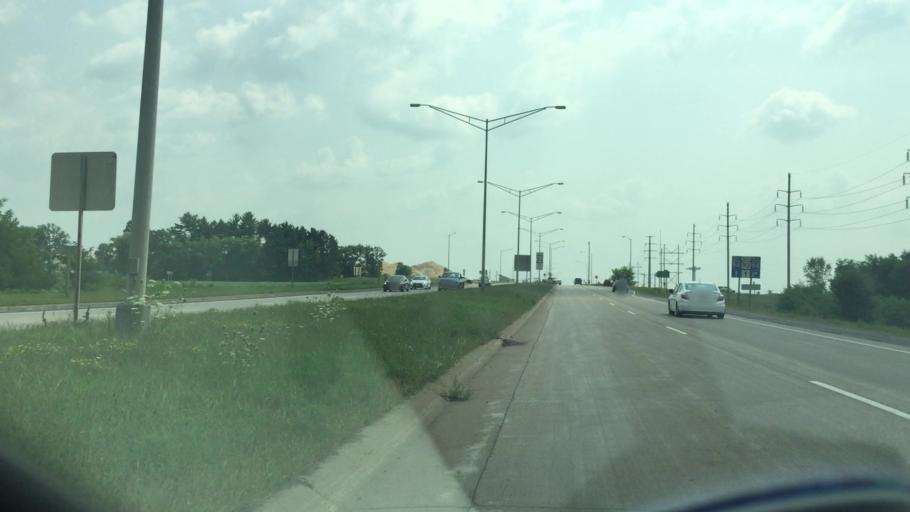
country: US
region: Wisconsin
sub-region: Eau Claire County
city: Altoona
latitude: 44.7691
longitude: -91.4593
